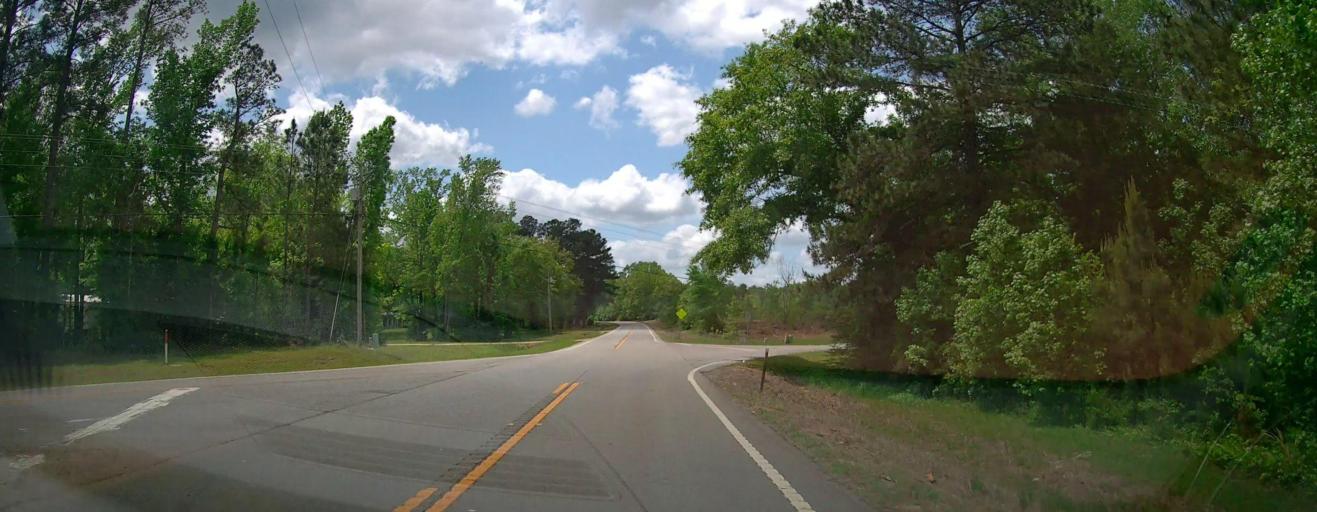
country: US
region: Georgia
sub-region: Laurens County
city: Dublin
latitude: 32.5991
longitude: -83.0106
